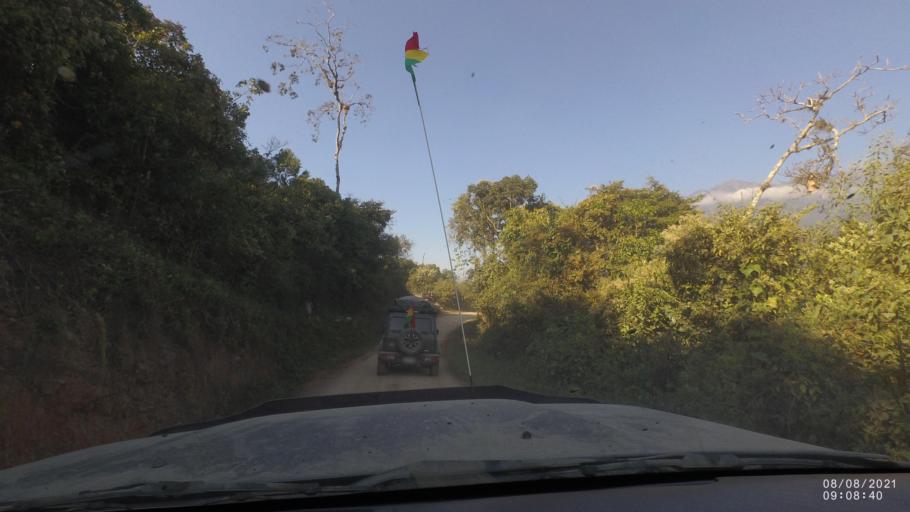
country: BO
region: La Paz
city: Quime
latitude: -16.5663
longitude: -66.7326
